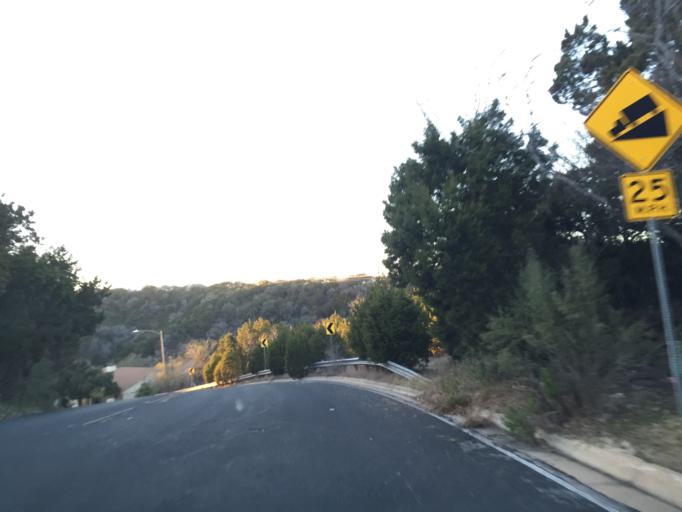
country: US
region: Texas
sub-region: Williamson County
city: Jollyville
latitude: 30.3982
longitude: -97.7602
